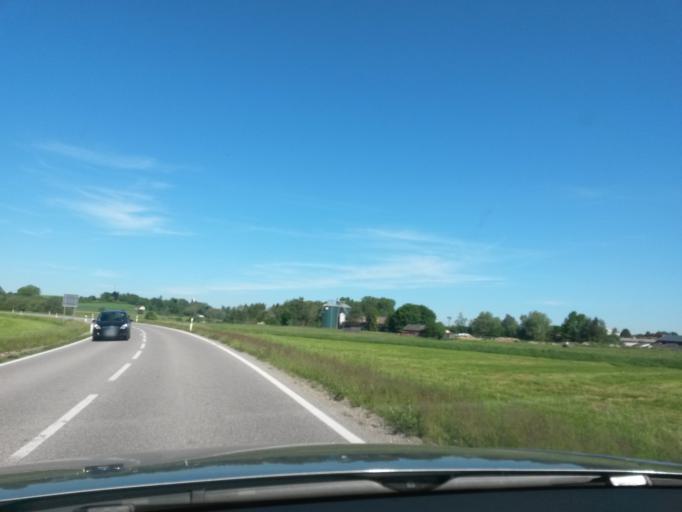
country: DE
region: Baden-Wuerttemberg
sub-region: Tuebingen Region
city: Bad Buchau
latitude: 48.0521
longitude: 9.6204
